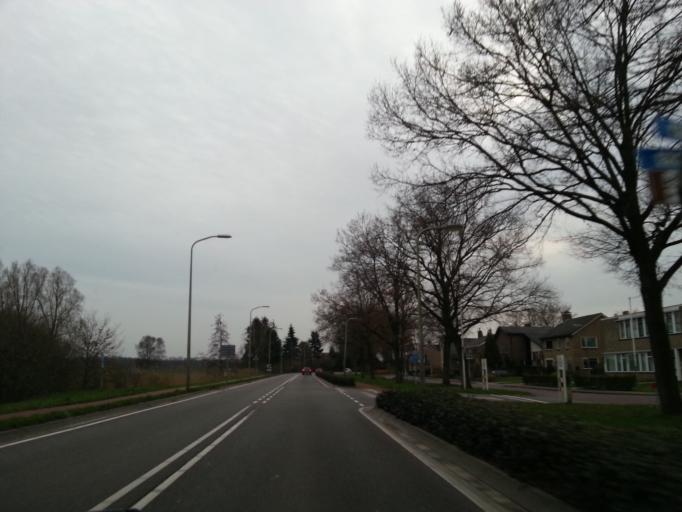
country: NL
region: Overijssel
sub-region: Gemeente Dalfsen
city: Dalfsen
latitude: 52.5061
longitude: 6.2634
